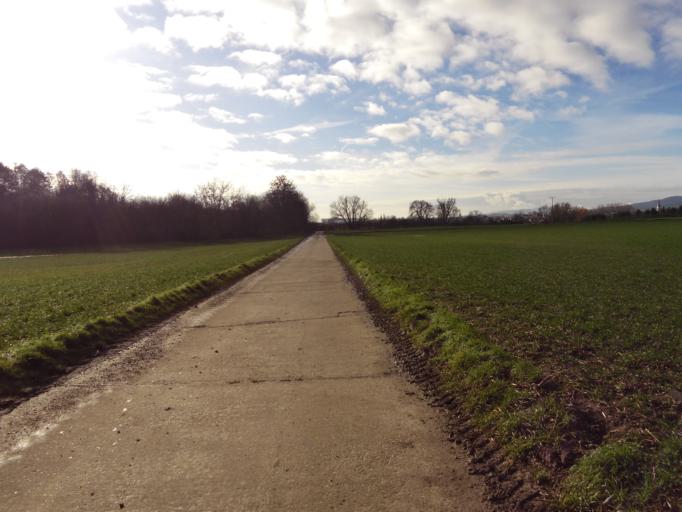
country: DE
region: Rheinland-Pfalz
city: Kirchheim an der Weinstrasse
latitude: 49.5488
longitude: 8.1891
